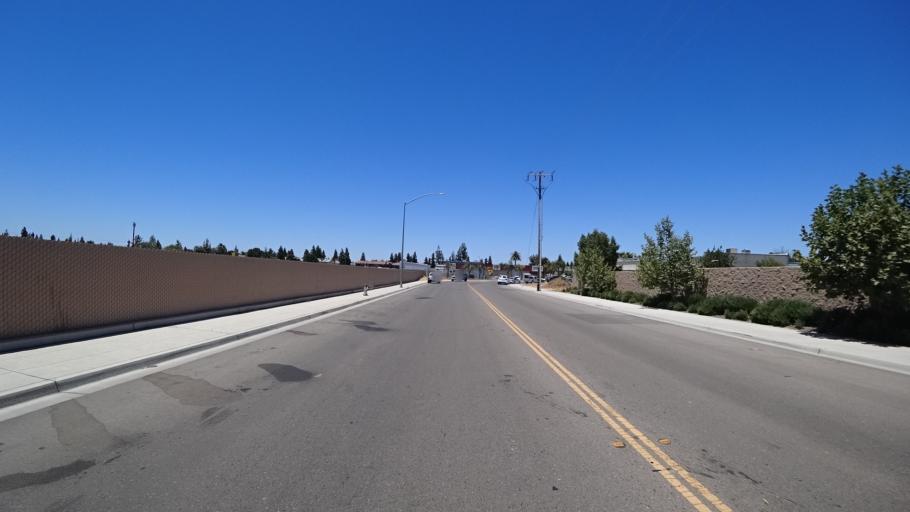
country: US
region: California
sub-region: Fresno County
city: West Park
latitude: 36.7684
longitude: -119.8395
